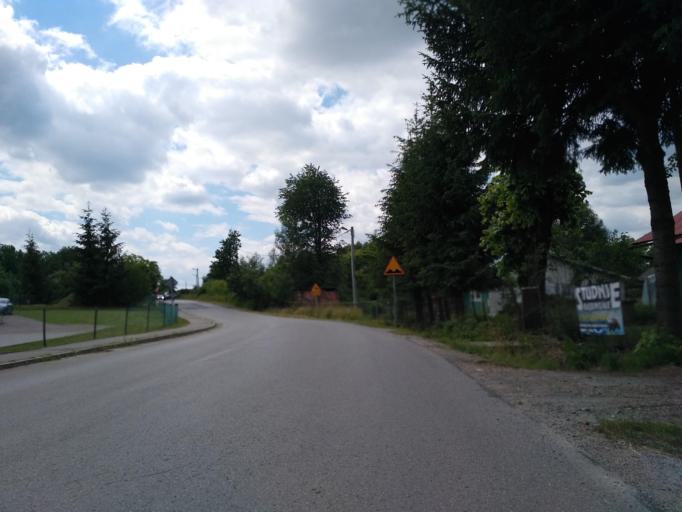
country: PL
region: Subcarpathian Voivodeship
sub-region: Powiat rzeszowski
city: Dynow
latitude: 49.7810
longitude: 22.2339
